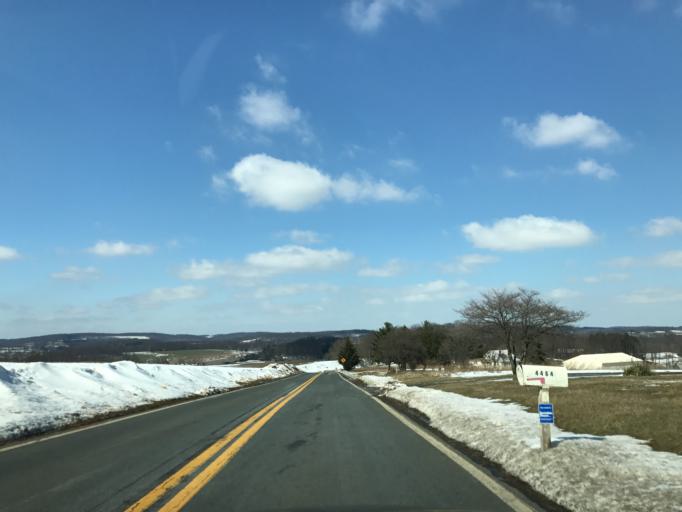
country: US
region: Maryland
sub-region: Carroll County
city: Manchester
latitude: 39.6966
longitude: -76.8381
